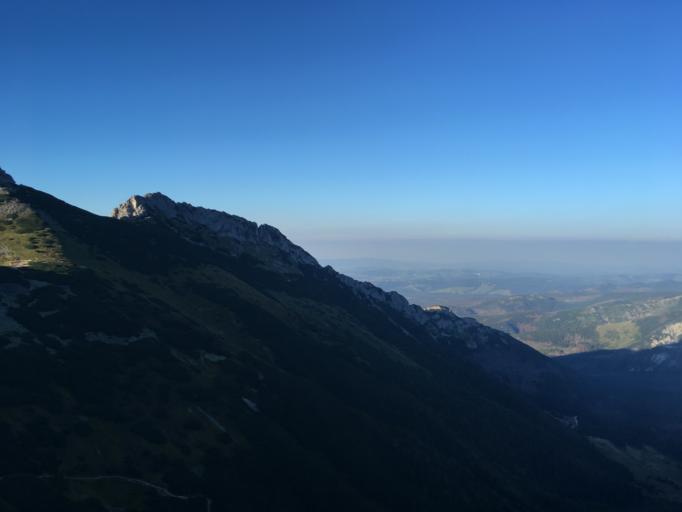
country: PL
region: Lesser Poland Voivodeship
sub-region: Powiat tatrzanski
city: Zakopane
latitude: 49.2444
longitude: 19.9322
